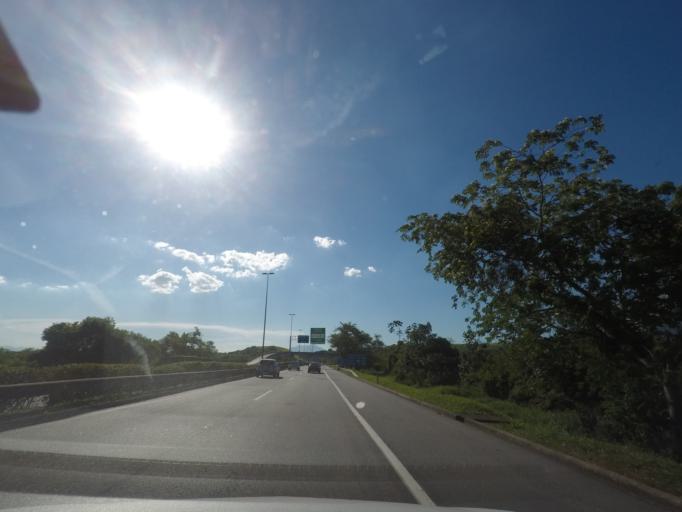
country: BR
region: Rio de Janeiro
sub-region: Petropolis
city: Petropolis
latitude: -22.6488
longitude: -43.1774
